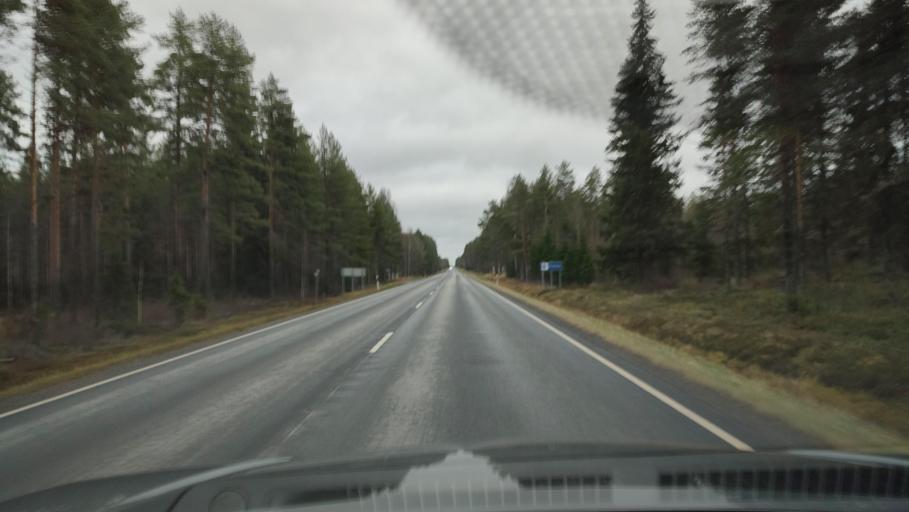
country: FI
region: Southern Ostrobothnia
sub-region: Seinaejoki
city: Kurikka
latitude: 62.5192
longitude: 22.3167
